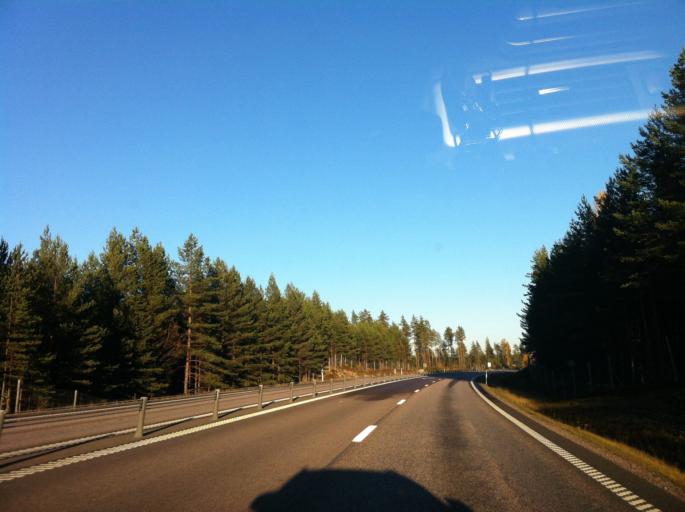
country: SE
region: Dalarna
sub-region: Hedemora Kommun
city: Langshyttan
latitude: 60.5675
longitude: 15.9592
